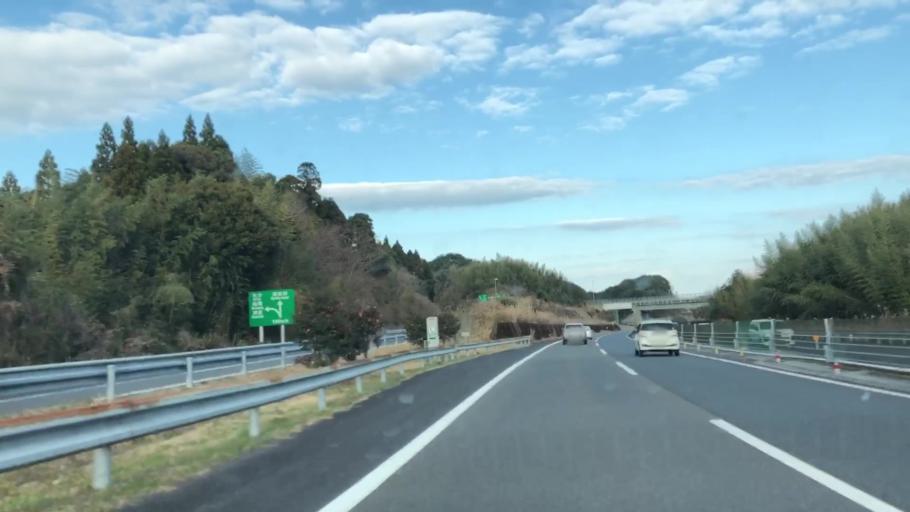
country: JP
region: Miyazaki
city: Miyazaki-shi
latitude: 31.8469
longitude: 131.3547
